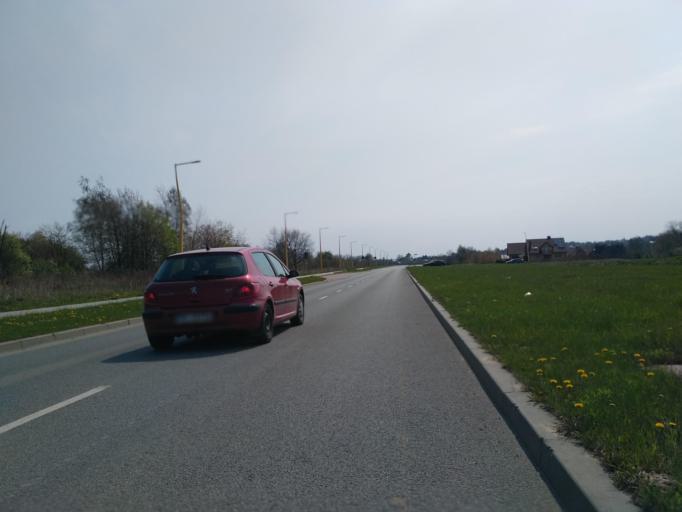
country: PL
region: Subcarpathian Voivodeship
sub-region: Krosno
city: Krosno
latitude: 49.6733
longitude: 21.7440
